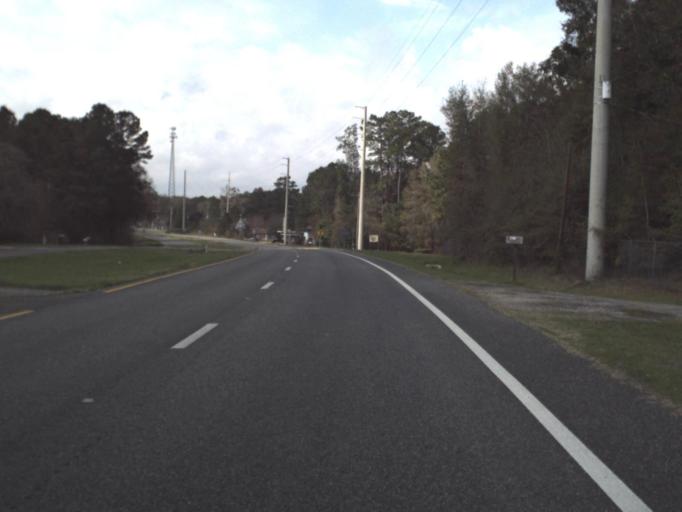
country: US
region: Florida
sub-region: Leon County
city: Tallahassee
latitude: 30.4229
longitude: -84.1123
